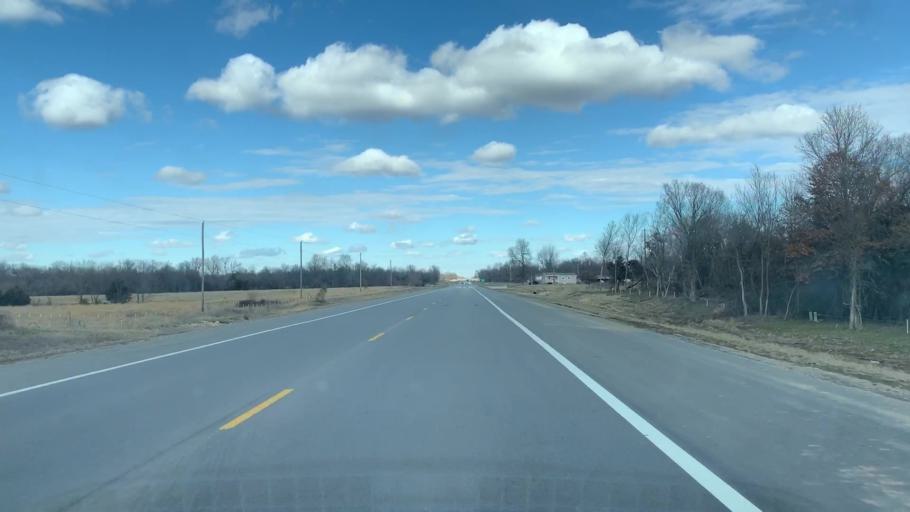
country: US
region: Kansas
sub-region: Cherokee County
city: Columbus
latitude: 37.2700
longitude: -94.8321
